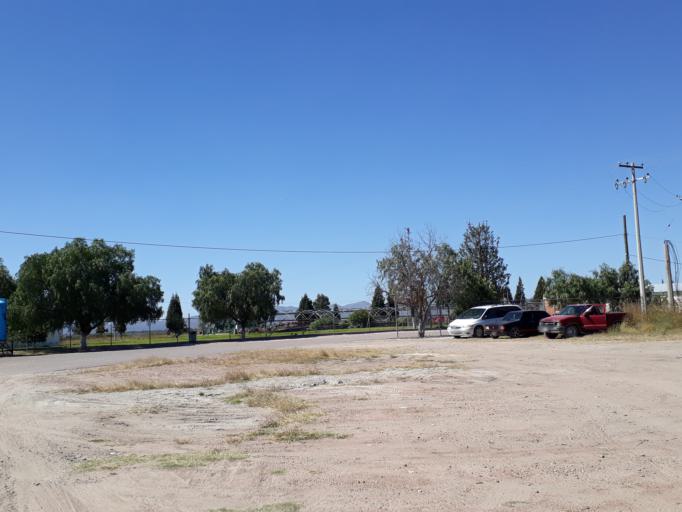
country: MX
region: Aguascalientes
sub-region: Aguascalientes
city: Penuelas (El Cienegal)
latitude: 21.7626
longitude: -102.2877
